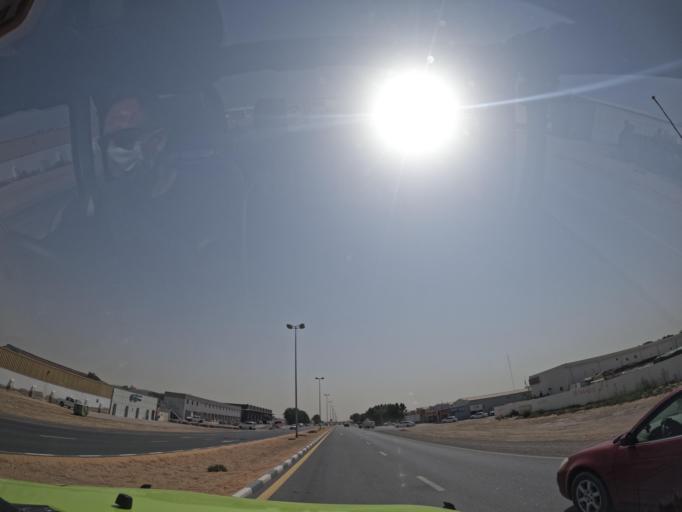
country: AE
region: Umm al Qaywayn
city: Umm al Qaywayn
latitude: 25.5042
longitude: 55.5608
